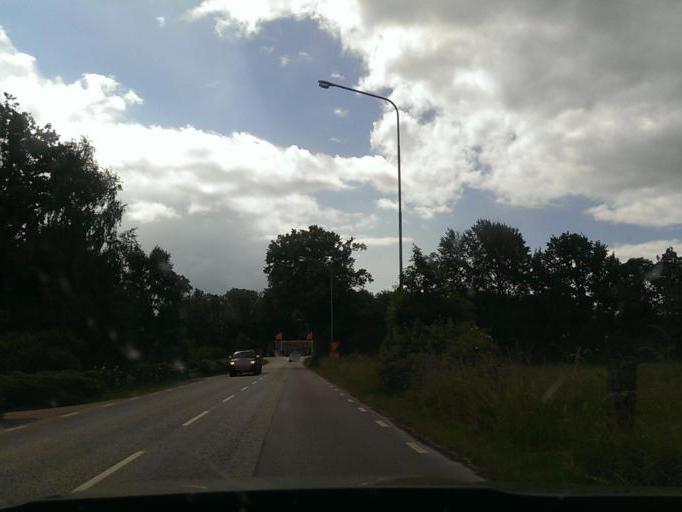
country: SE
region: Skane
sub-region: Eslovs Kommun
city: Stehag
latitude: 55.9390
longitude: 13.3824
